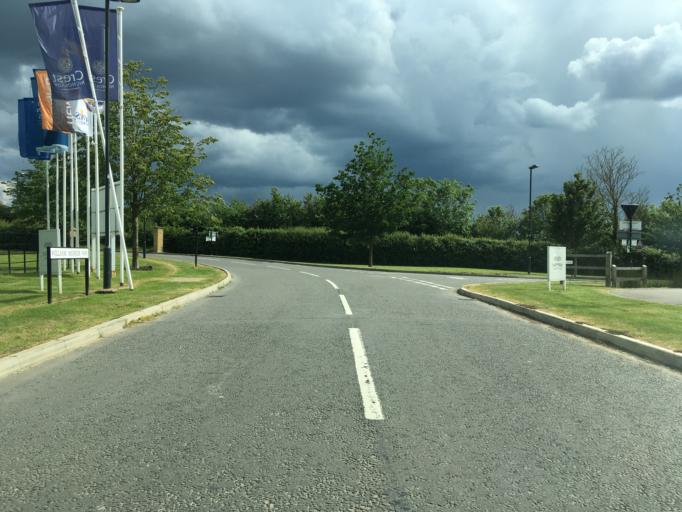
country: GB
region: England
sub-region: Borough of Swindon
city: Broad Blunsdon
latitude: 51.6070
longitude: -1.8153
